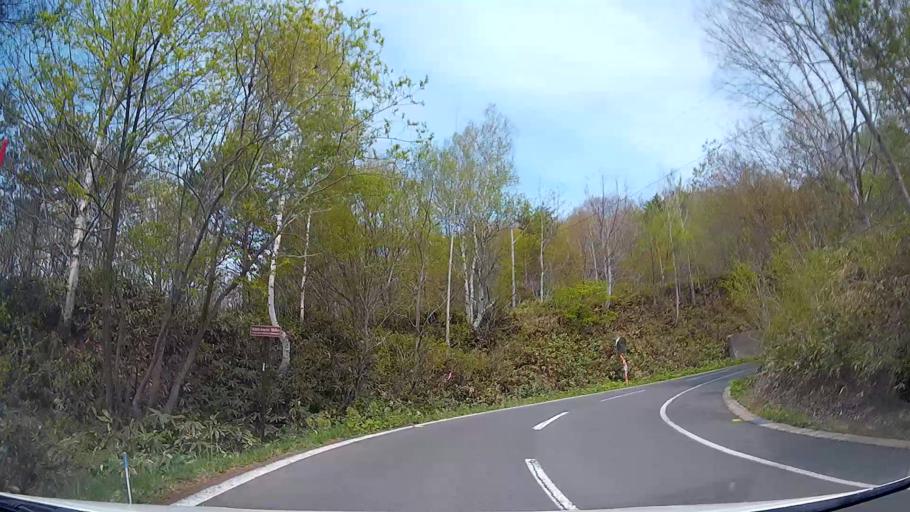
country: JP
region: Iwate
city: Shizukuishi
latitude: 39.9242
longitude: 140.9672
